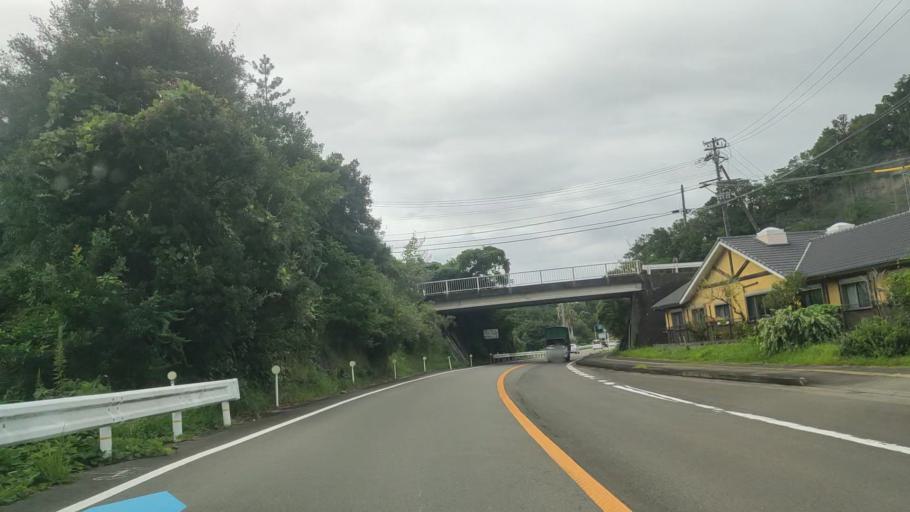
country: JP
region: Wakayama
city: Tanabe
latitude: 33.6943
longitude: 135.3883
